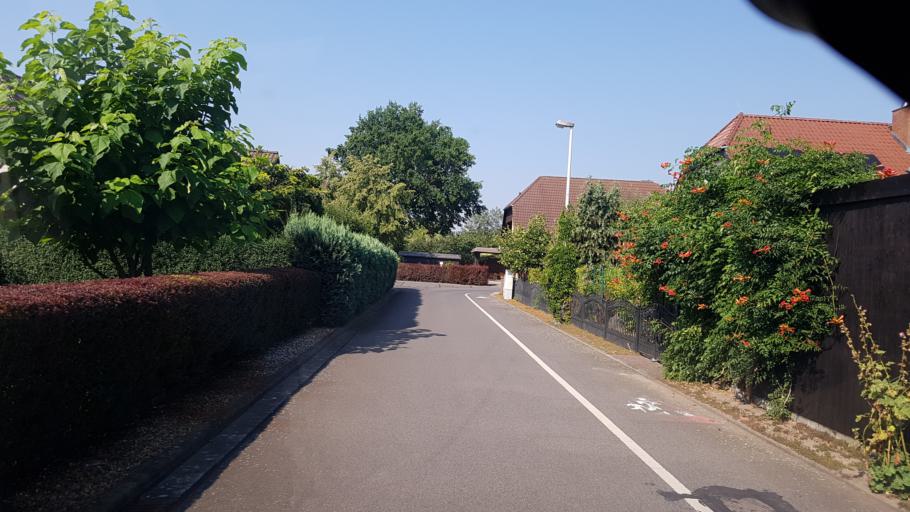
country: DE
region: Brandenburg
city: Cottbus
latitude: 51.7212
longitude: 14.4193
